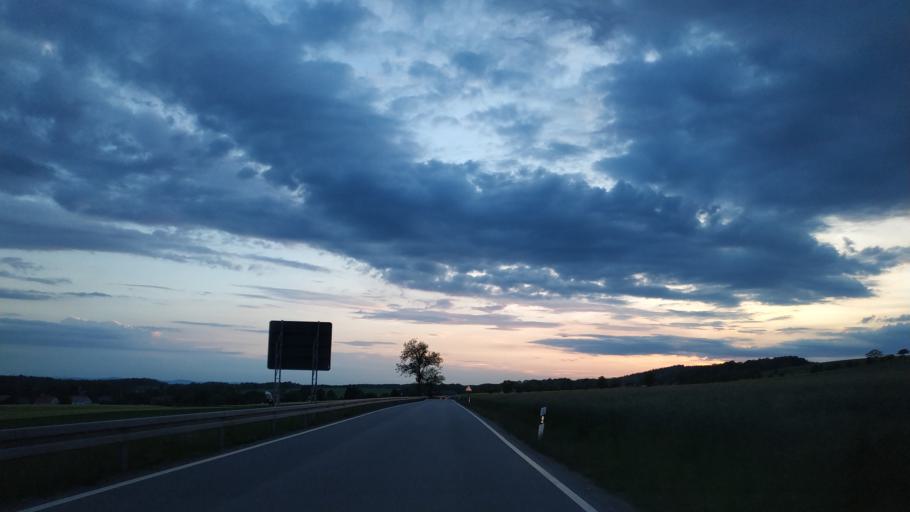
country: DE
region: Saxony
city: Hohnstein
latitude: 50.9850
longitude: 14.0871
